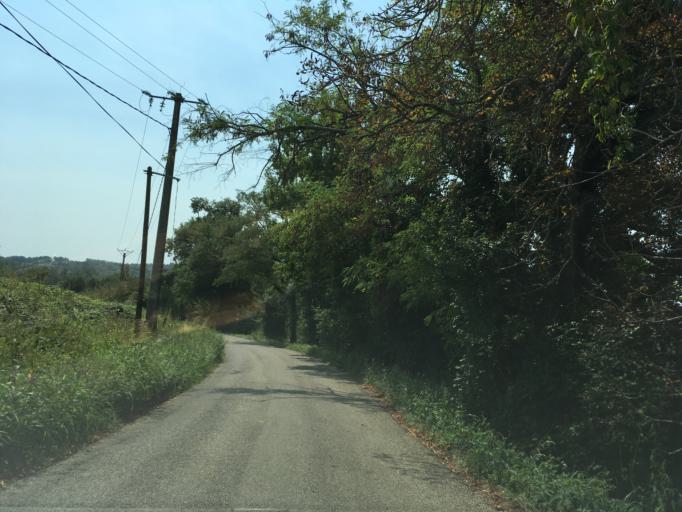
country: FR
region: Midi-Pyrenees
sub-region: Departement du Tarn-et-Garonne
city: Saint-Nauphary
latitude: 43.9889
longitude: 1.4003
